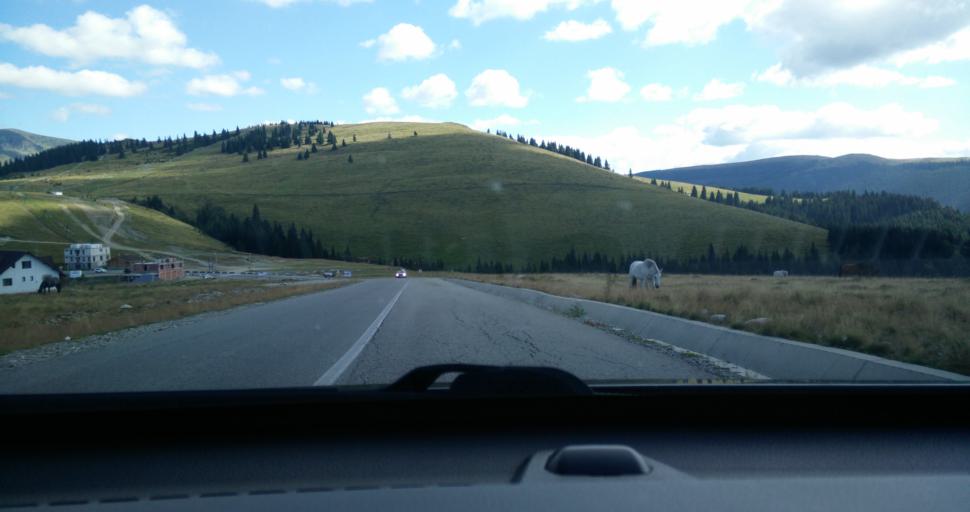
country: RO
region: Gorj
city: Novaci-Straini
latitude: 45.2730
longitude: 23.6882
